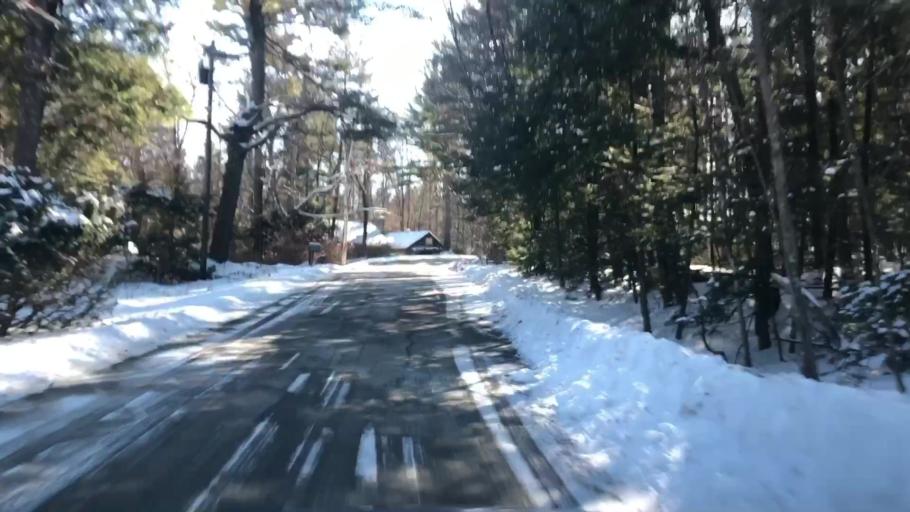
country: US
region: New Hampshire
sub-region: Hillsborough County
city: Bedford
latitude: 42.9408
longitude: -71.5356
